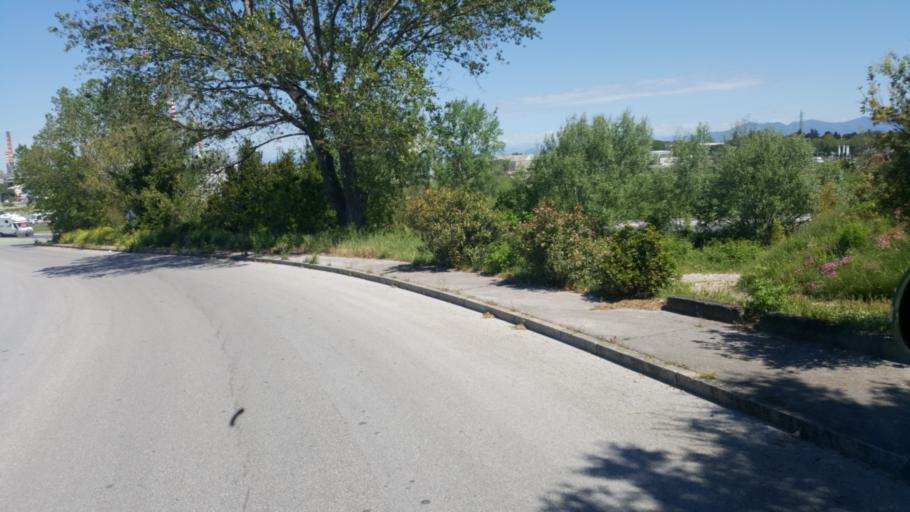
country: IT
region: Tuscany
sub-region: Provincia di Livorno
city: Livorno
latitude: 43.5744
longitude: 10.3442
